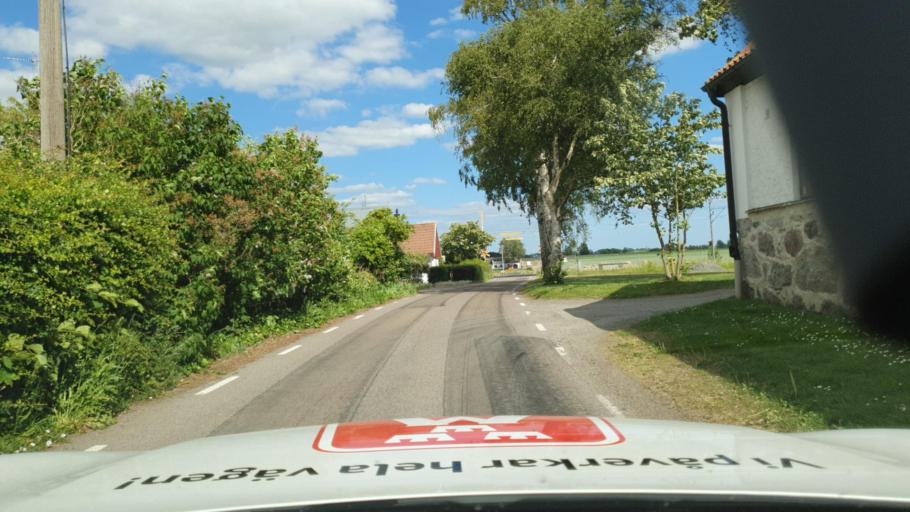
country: SE
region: Skane
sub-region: Ystads Kommun
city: Kopingebro
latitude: 55.4715
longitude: 13.9477
